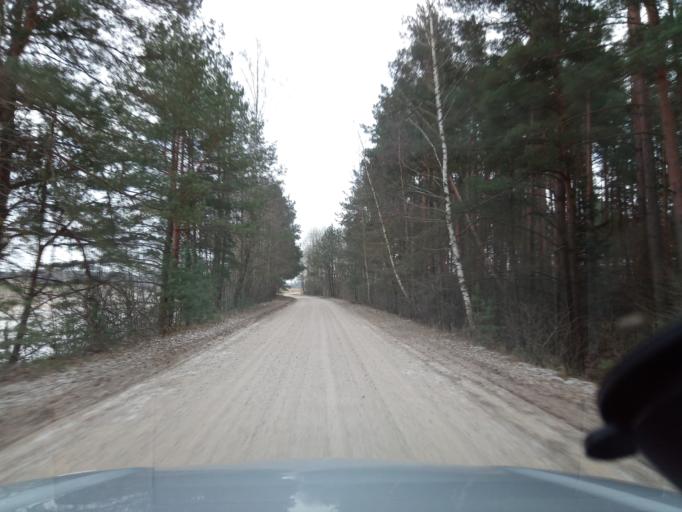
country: LT
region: Alytaus apskritis
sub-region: Alytaus rajonas
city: Daugai
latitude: 54.3185
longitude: 24.3362
